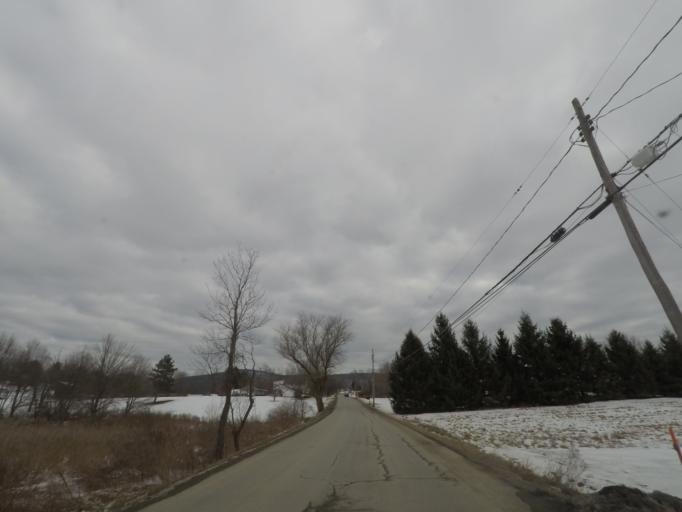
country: US
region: New York
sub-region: Rensselaer County
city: Poestenkill
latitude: 42.7342
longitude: -73.5792
